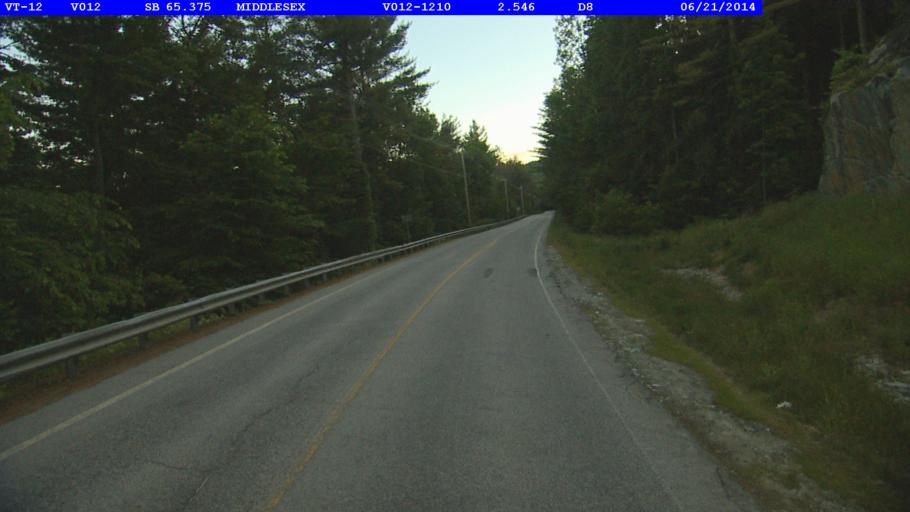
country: US
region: Vermont
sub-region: Washington County
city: Montpelier
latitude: 44.3375
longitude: -72.5684
